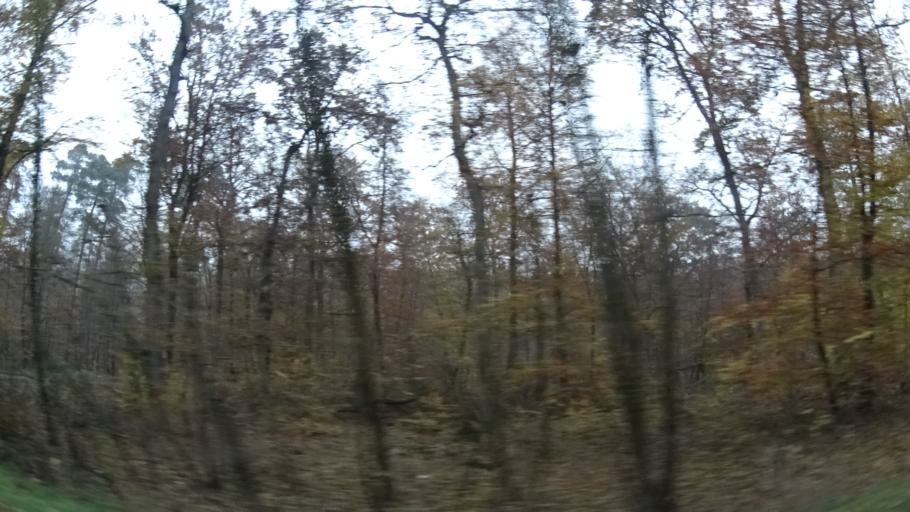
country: DE
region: Baden-Wuerttemberg
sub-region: Karlsruhe Region
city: Kronau
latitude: 49.2310
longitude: 8.5888
